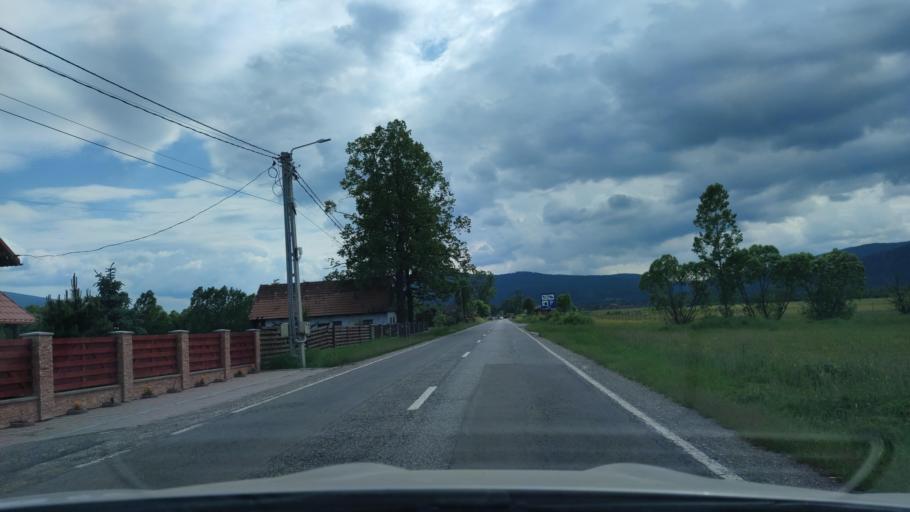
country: RO
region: Harghita
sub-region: Comuna Joseni
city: Joseni
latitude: 46.6851
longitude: 25.4117
